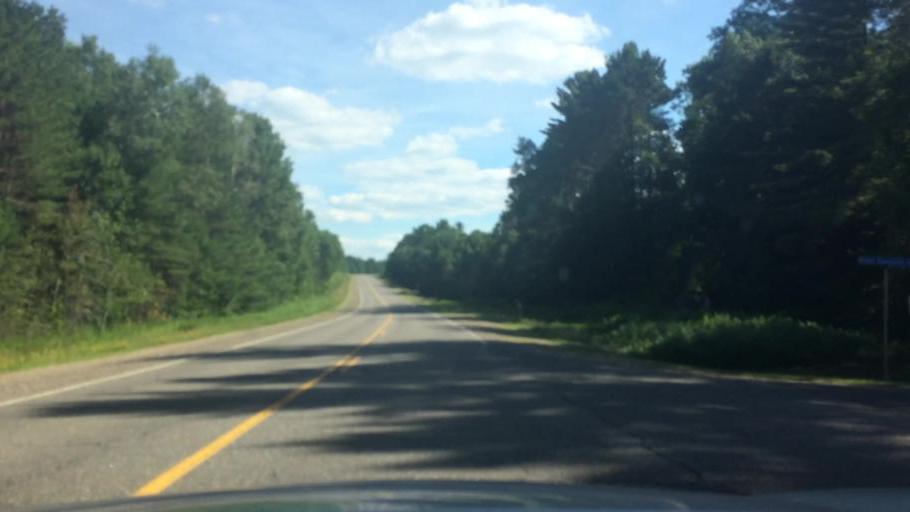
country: US
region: Wisconsin
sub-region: Vilas County
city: Lac du Flambeau
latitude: 46.0470
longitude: -89.6500
